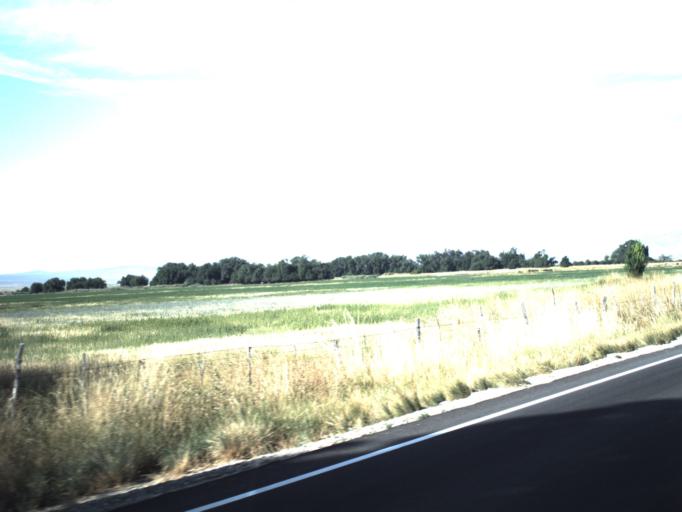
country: US
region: Idaho
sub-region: Cassia County
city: Burley
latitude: 41.8171
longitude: -113.3131
